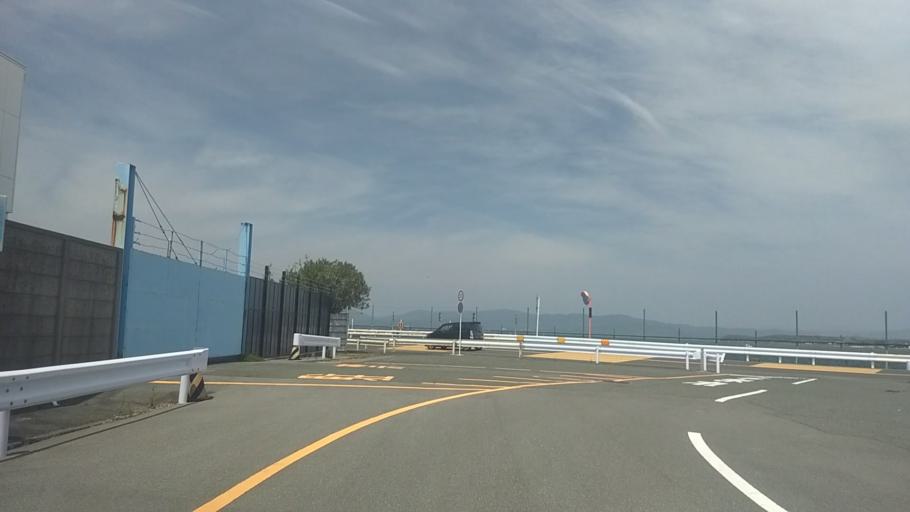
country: JP
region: Shizuoka
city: Kosai-shi
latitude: 34.7007
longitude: 137.5745
